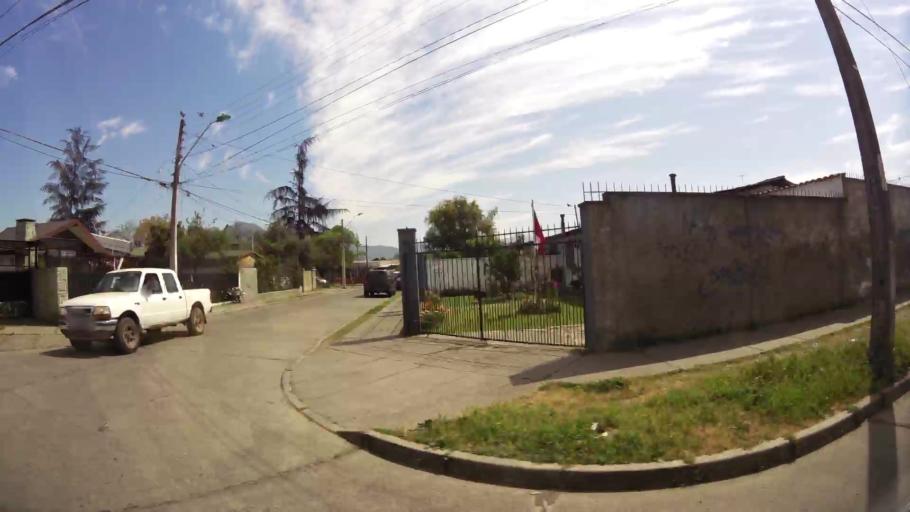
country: CL
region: Santiago Metropolitan
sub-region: Provincia de Talagante
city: Talagante
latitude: -33.6643
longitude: -70.9224
